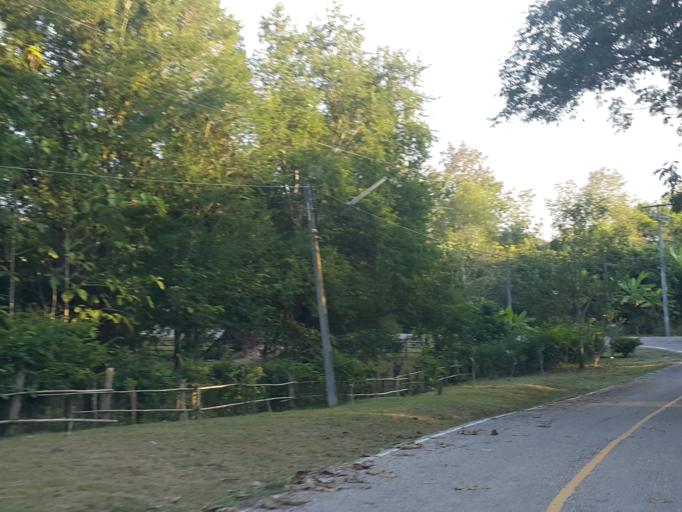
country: TH
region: Lampang
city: Lampang
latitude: 18.4395
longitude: 99.5732
